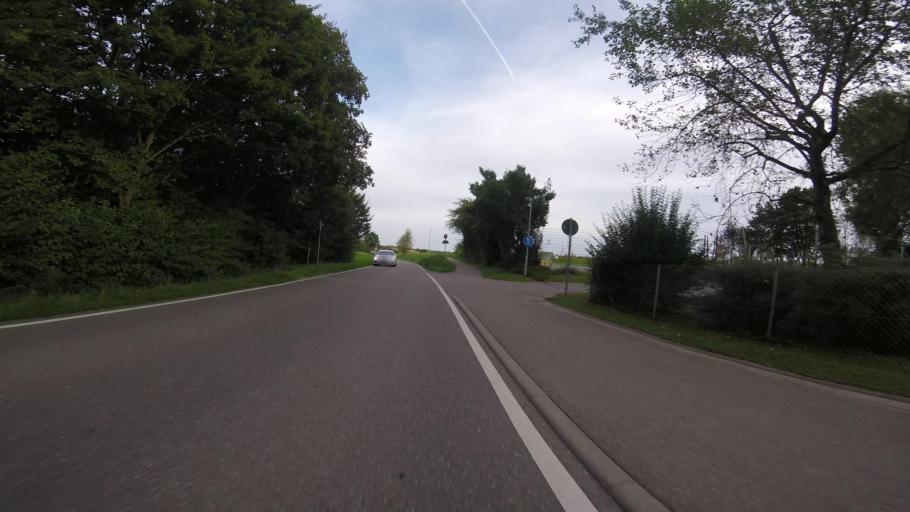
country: DE
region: Baden-Wuerttemberg
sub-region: Regierungsbezirk Stuttgart
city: Aspach
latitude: 48.9765
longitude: 9.3965
